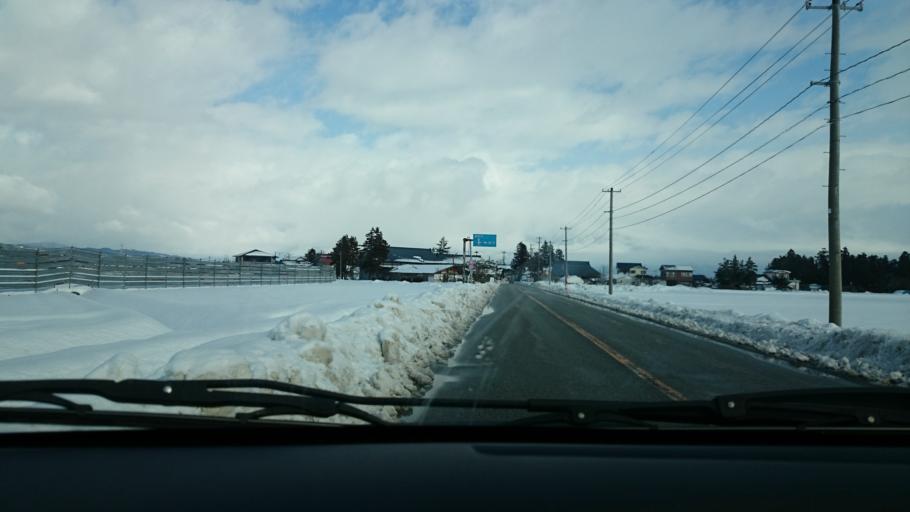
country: JP
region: Fukushima
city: Kitakata
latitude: 37.5761
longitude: 139.8316
